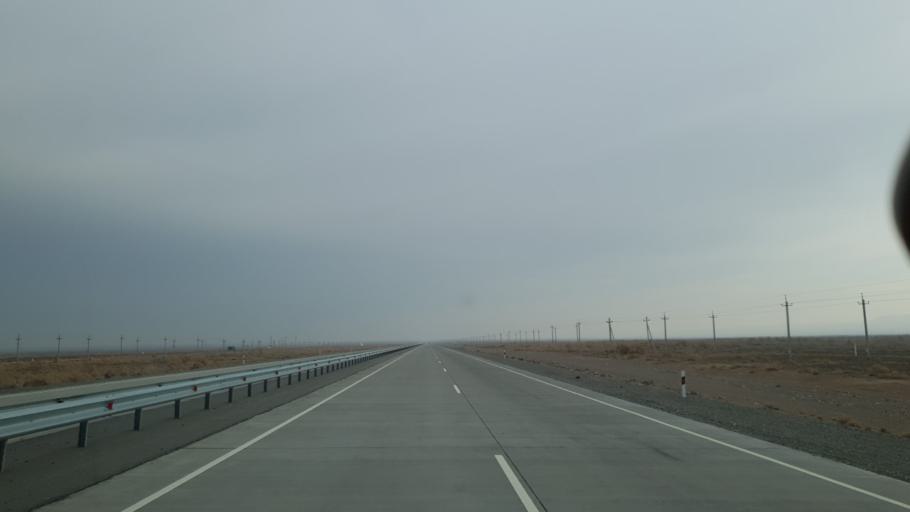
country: KZ
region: Almaty Oblysy
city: Kegen
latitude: 43.7293
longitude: 78.7782
